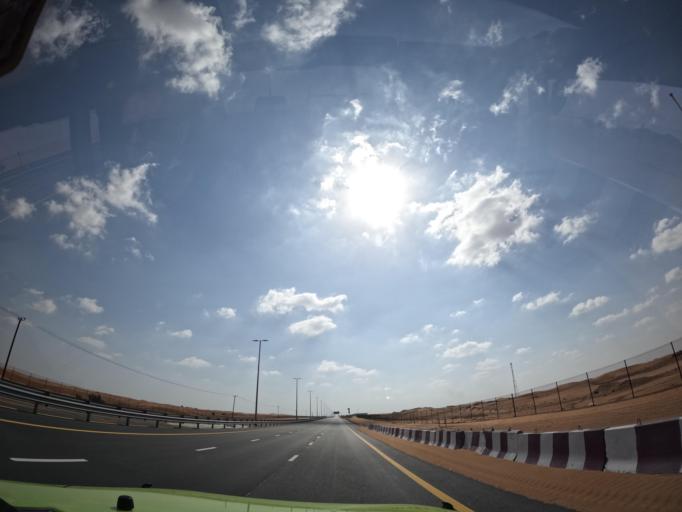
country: AE
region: Ash Shariqah
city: Adh Dhayd
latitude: 24.9741
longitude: 55.6871
